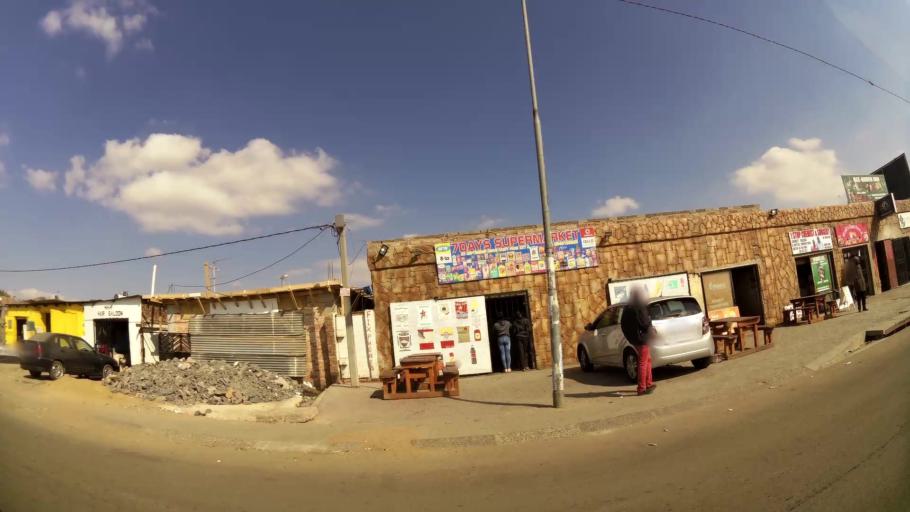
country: ZA
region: Gauteng
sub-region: Ekurhuleni Metropolitan Municipality
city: Tembisa
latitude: -26.0053
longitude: 28.1803
